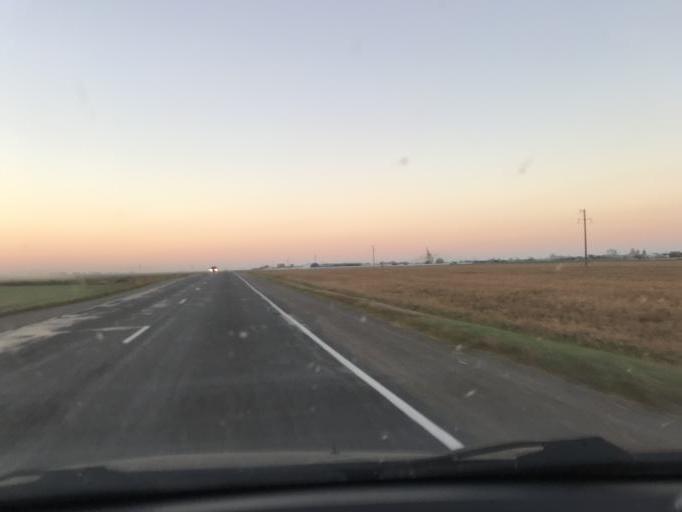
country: BY
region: Gomel
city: Horad Rechytsa
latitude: 52.2399
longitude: 30.5039
